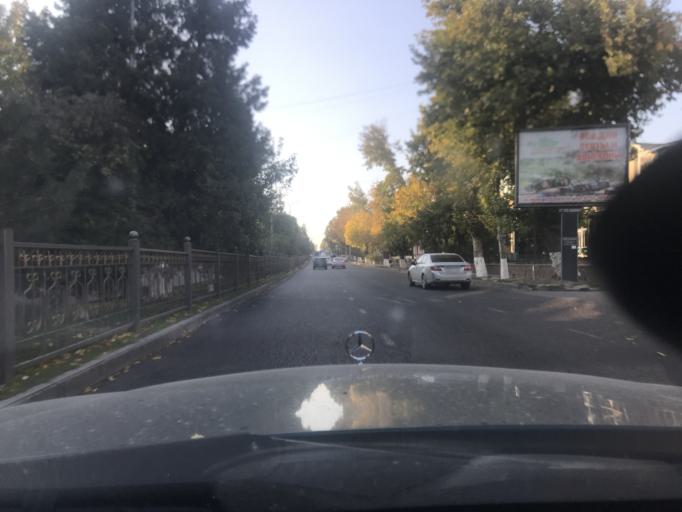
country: KZ
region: Ongtustik Qazaqstan
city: Shymkent
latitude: 42.3001
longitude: 69.6083
